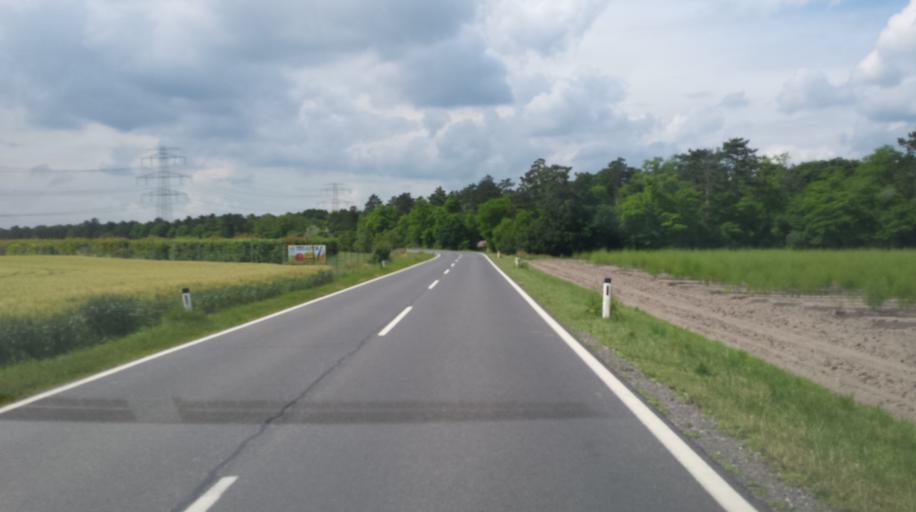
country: AT
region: Lower Austria
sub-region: Politischer Bezirk Ganserndorf
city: Deutsch-Wagram
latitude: 48.3028
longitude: 16.5451
